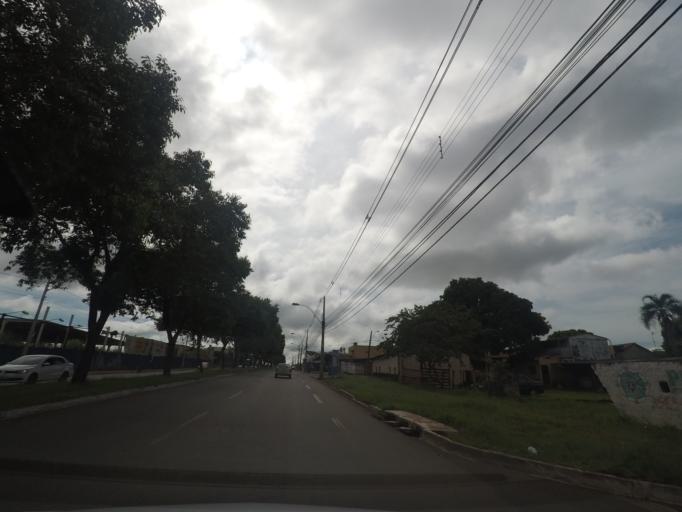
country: BR
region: Goias
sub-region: Goiania
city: Goiania
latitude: -16.6583
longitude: -49.1968
